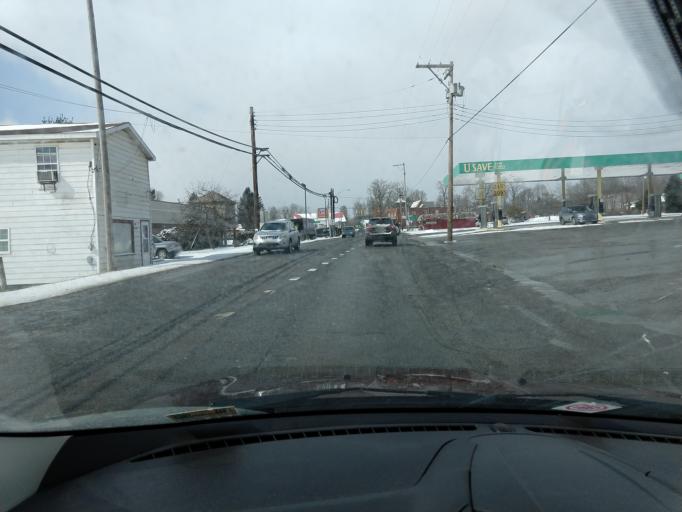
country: US
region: West Virginia
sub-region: Nicholas County
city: Craigsville
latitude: 38.3302
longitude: -80.6516
